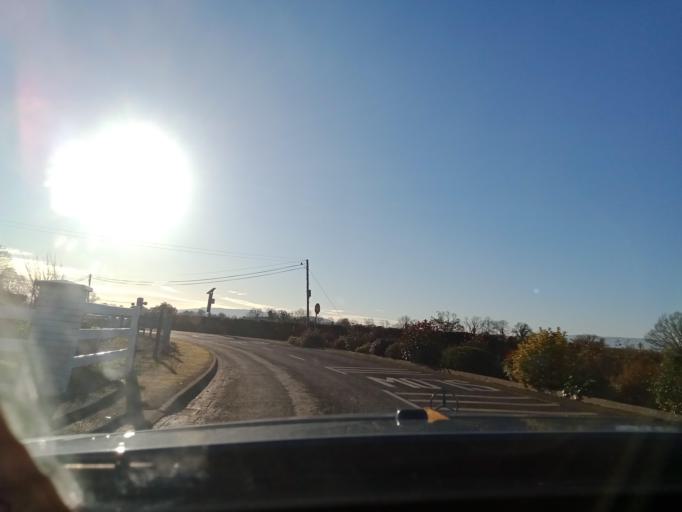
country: IE
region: Leinster
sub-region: Kilkenny
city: Piltown
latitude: 52.3859
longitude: -7.3450
